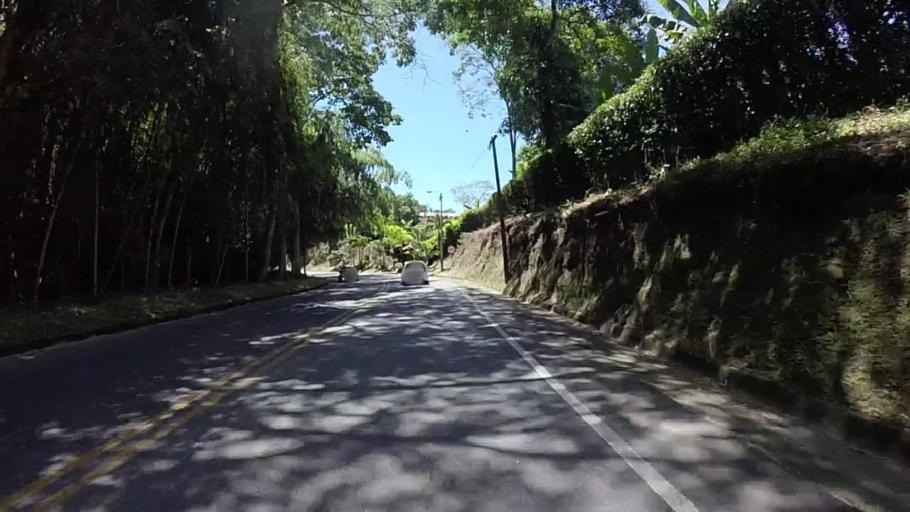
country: CO
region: Valle del Cauca
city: Alcala
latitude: 4.6996
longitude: -75.8303
